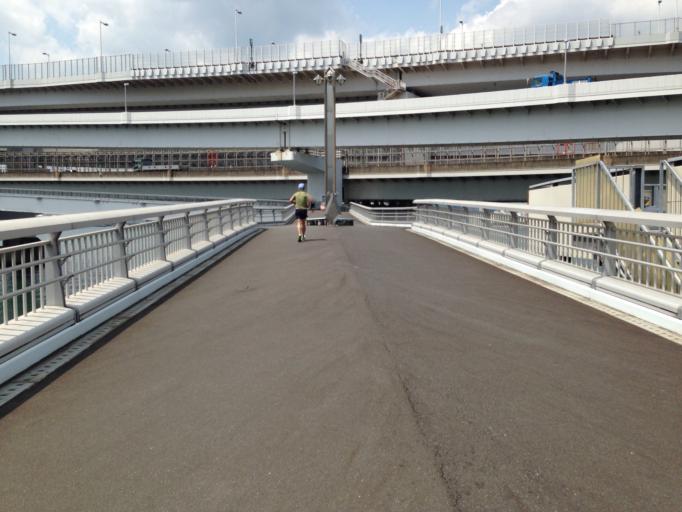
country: JP
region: Tokyo
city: Tokyo
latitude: 35.6354
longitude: 139.7754
